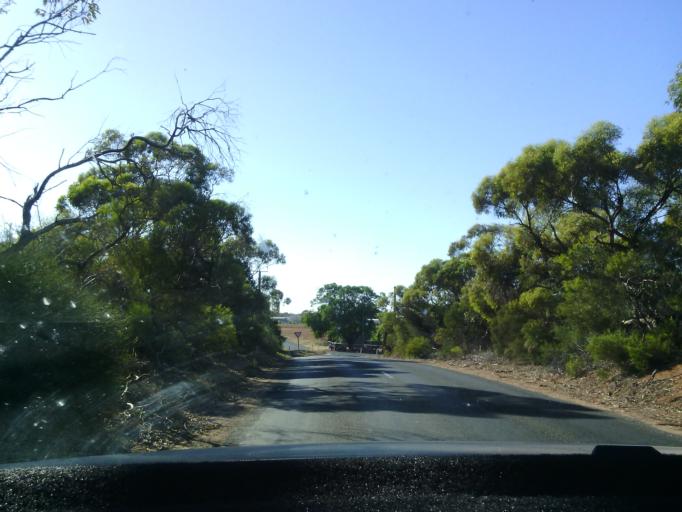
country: AU
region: South Australia
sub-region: Berri and Barmera
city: Berri
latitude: -34.2643
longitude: 140.5966
